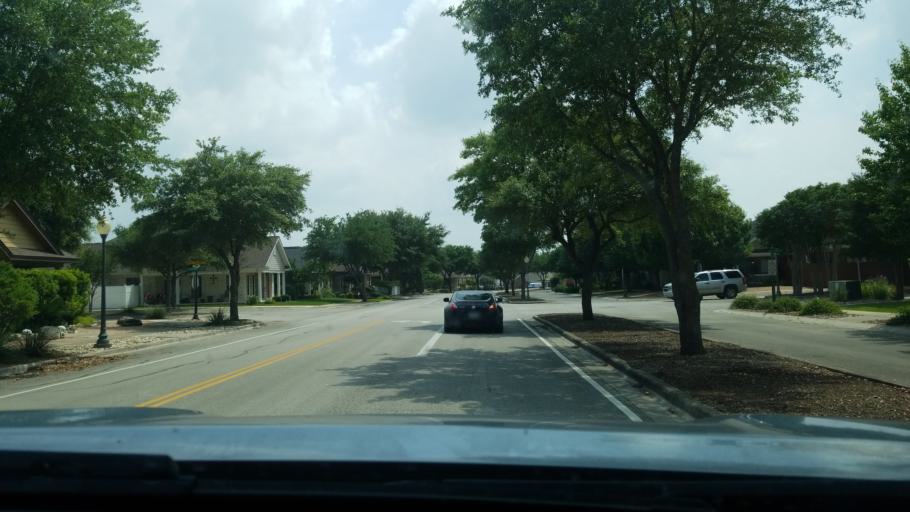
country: US
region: Texas
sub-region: Comal County
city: New Braunfels
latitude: 29.7297
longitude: -98.0988
